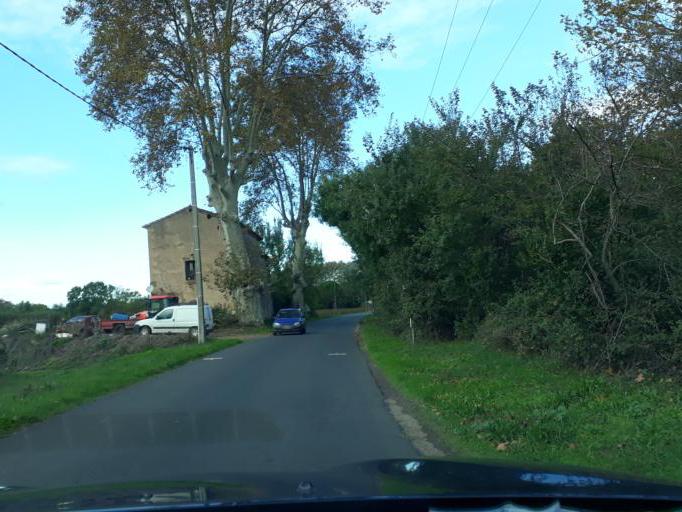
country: FR
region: Languedoc-Roussillon
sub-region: Departement de l'Herault
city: Bessan
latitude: 43.3516
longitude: 3.4303
